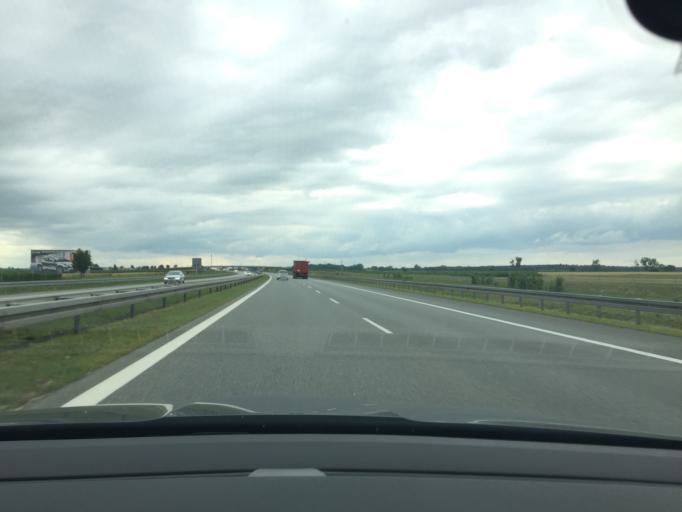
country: PL
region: Greater Poland Voivodeship
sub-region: Powiat poznanski
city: Buk
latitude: 52.3889
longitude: 16.4639
